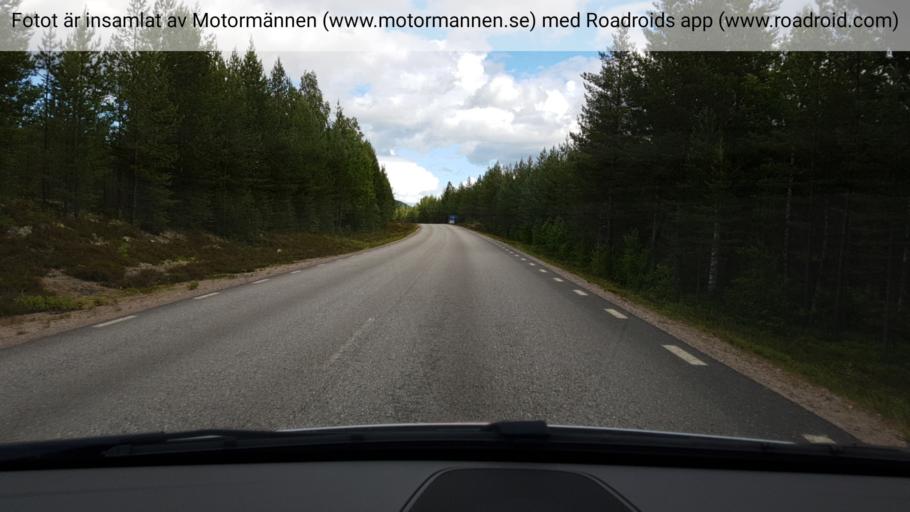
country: SE
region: Jaemtland
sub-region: Harjedalens Kommun
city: Sveg
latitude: 62.0150
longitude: 14.8666
